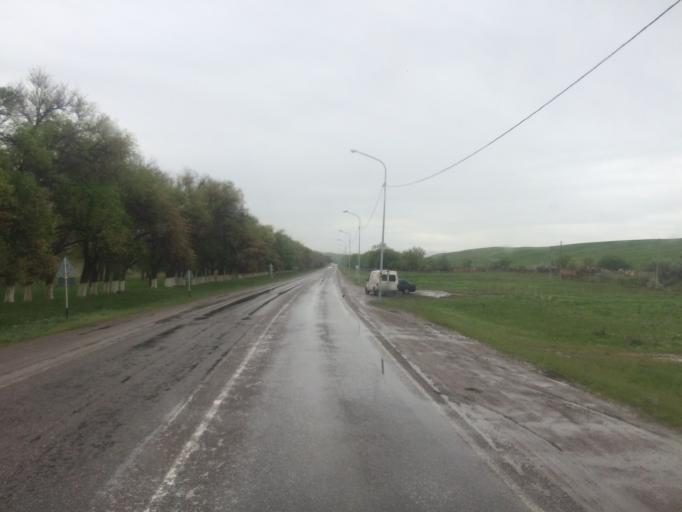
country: KZ
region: Zhambyl
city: Georgiyevka
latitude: 43.2372
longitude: 74.7615
